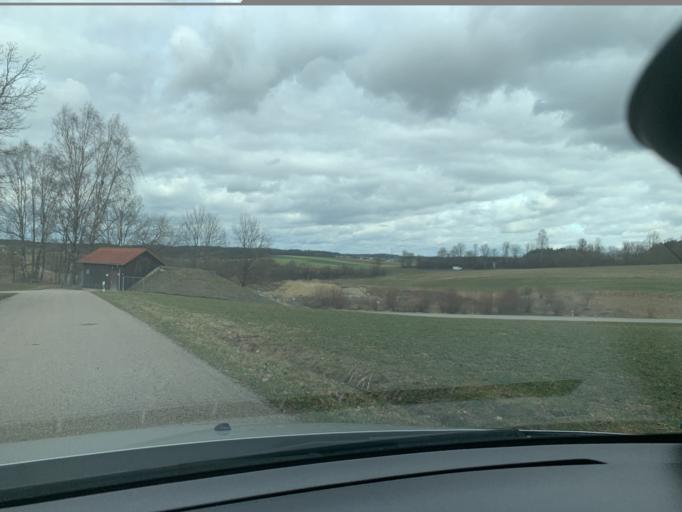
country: DE
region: Bavaria
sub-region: Lower Bavaria
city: Geisenhausen
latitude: 48.4713
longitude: 12.2745
